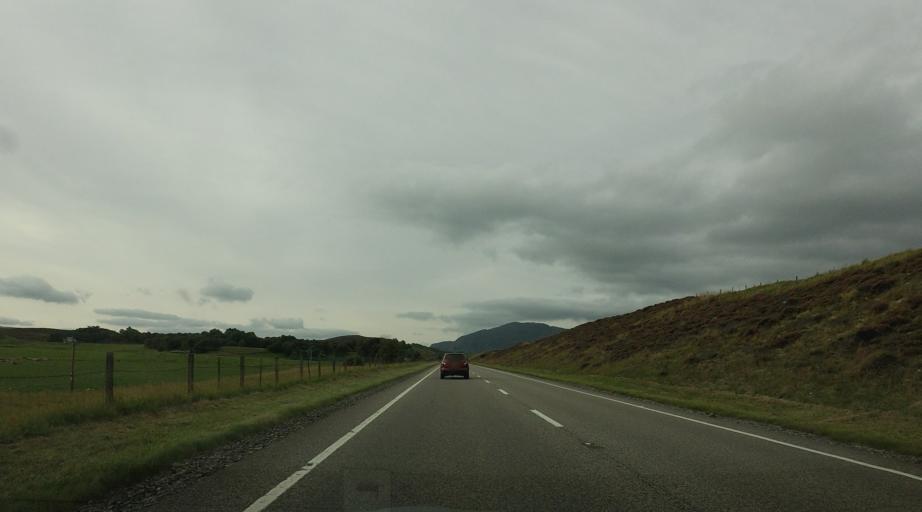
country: GB
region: Scotland
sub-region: Highland
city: Kingussie
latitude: 57.0617
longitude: -4.0822
